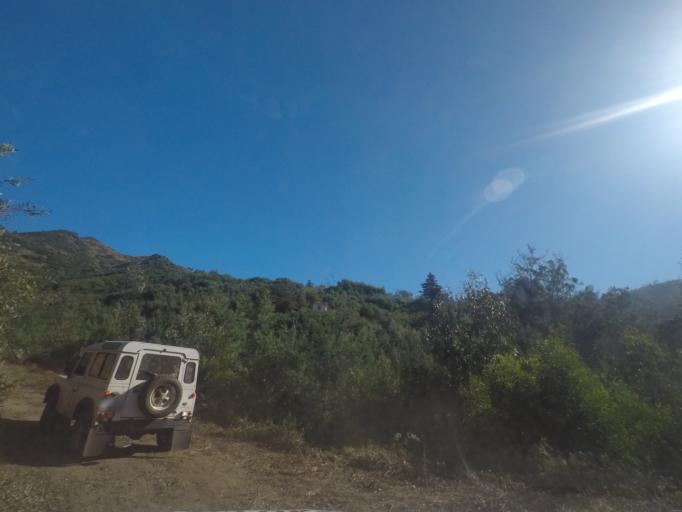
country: PT
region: Madeira
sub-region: Funchal
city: Nossa Senhora do Monte
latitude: 32.6945
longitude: -16.9104
